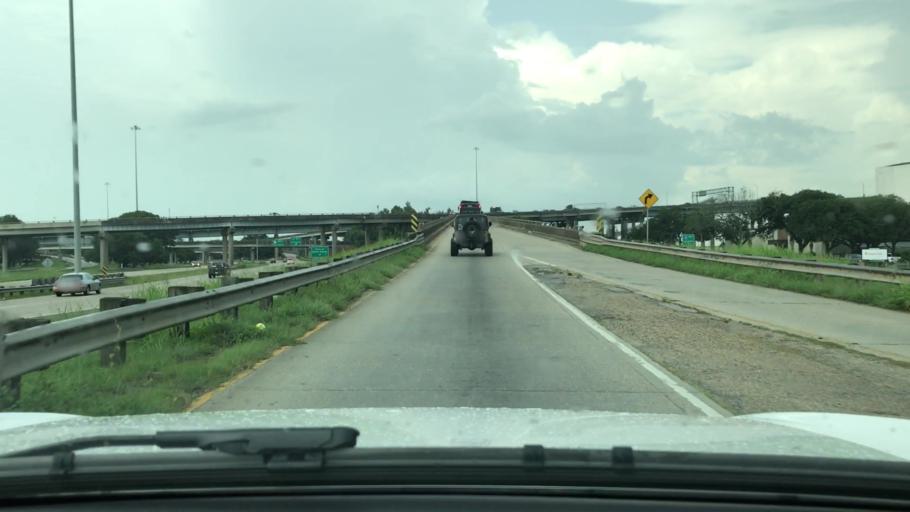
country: US
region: Louisiana
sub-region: West Baton Rouge Parish
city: Port Allen
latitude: 30.4366
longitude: -91.2088
